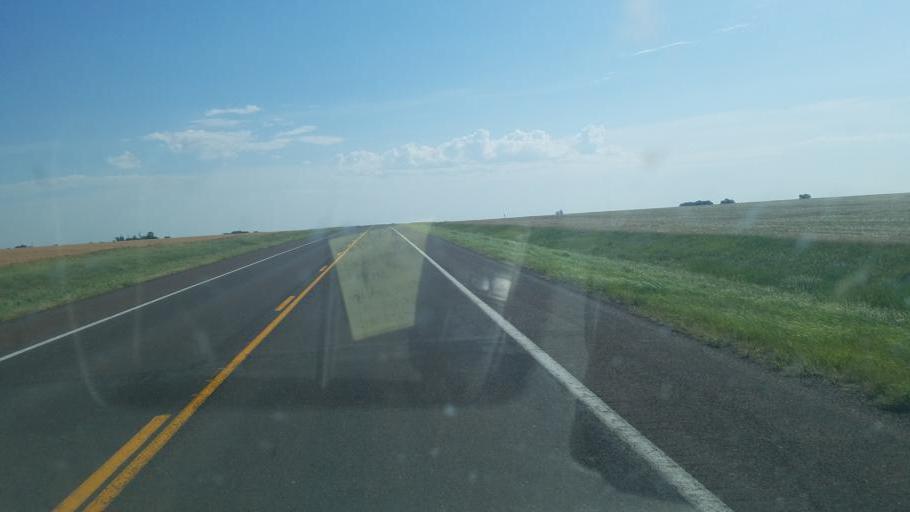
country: US
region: Kansas
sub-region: Barton County
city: Ellinwood
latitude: 38.5737
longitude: -98.4400
